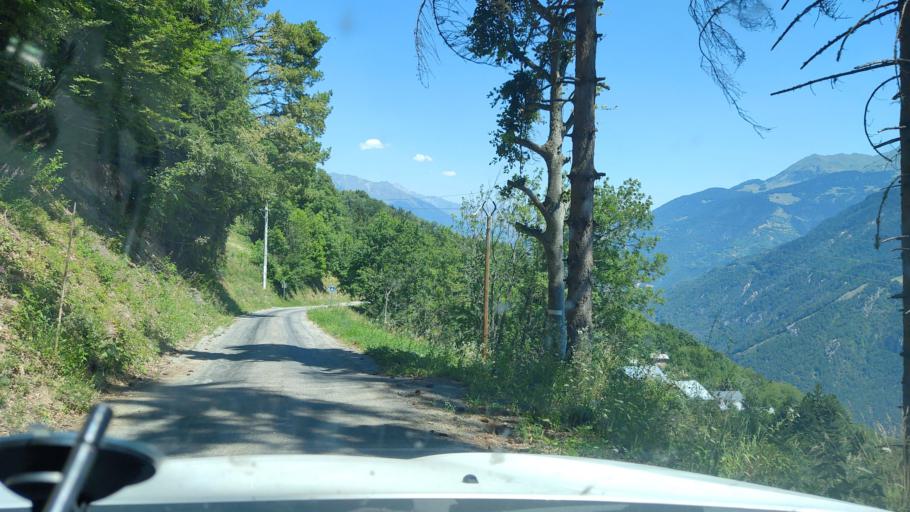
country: FR
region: Rhone-Alpes
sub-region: Departement de la Savoie
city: Salins-les-Thermes
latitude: 45.4673
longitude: 6.5087
